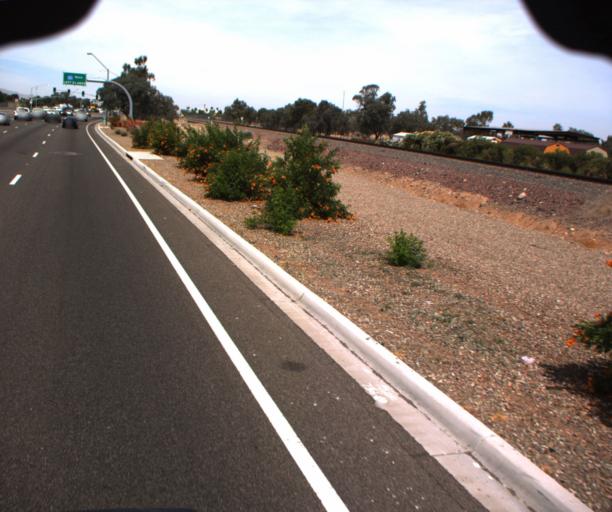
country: US
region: Arizona
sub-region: Maricopa County
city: Sun City
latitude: 33.5935
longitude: -112.2580
